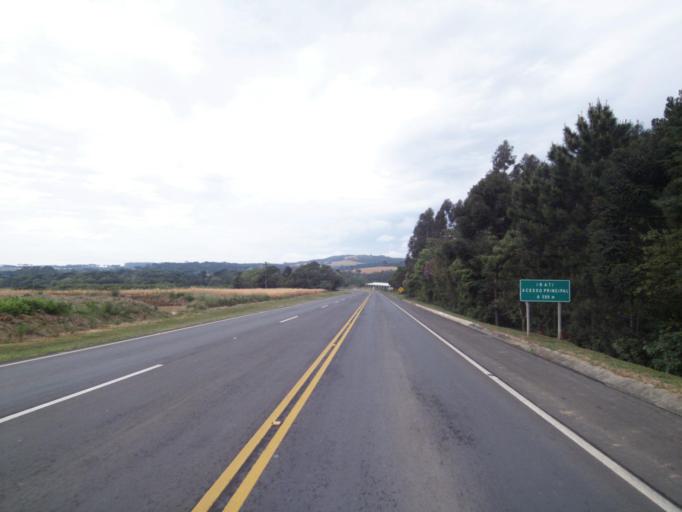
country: BR
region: Parana
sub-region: Irati
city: Irati
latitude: -25.4544
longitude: -50.6295
